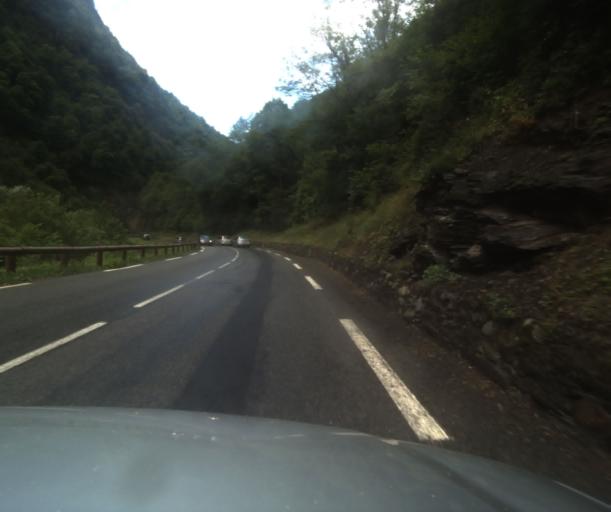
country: FR
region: Midi-Pyrenees
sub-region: Departement des Hautes-Pyrenees
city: Pierrefitte-Nestalas
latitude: 42.9391
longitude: -0.0506
